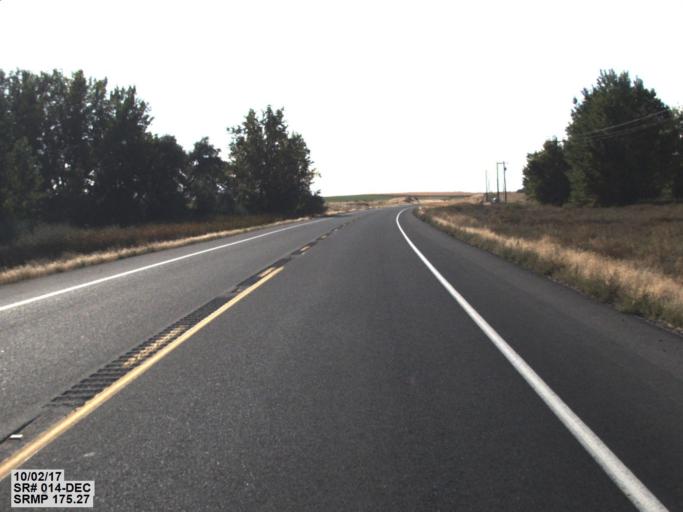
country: US
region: Oregon
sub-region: Morrow County
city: Irrigon
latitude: 45.9489
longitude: -119.4379
